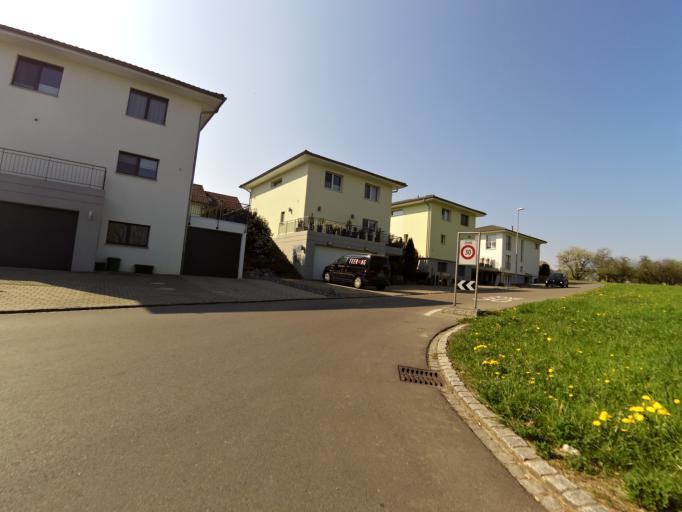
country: CH
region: Thurgau
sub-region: Frauenfeld District
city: Gachnang
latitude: 47.5514
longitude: 8.8625
